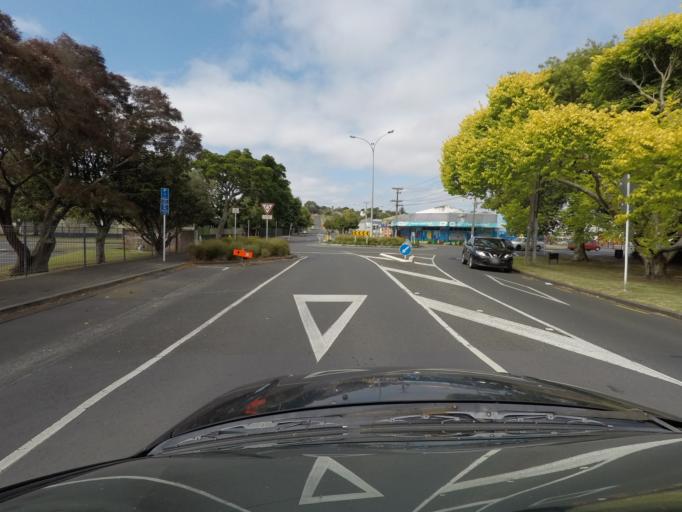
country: NZ
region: Auckland
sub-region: Auckland
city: Auckland
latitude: -36.9121
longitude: 174.7483
